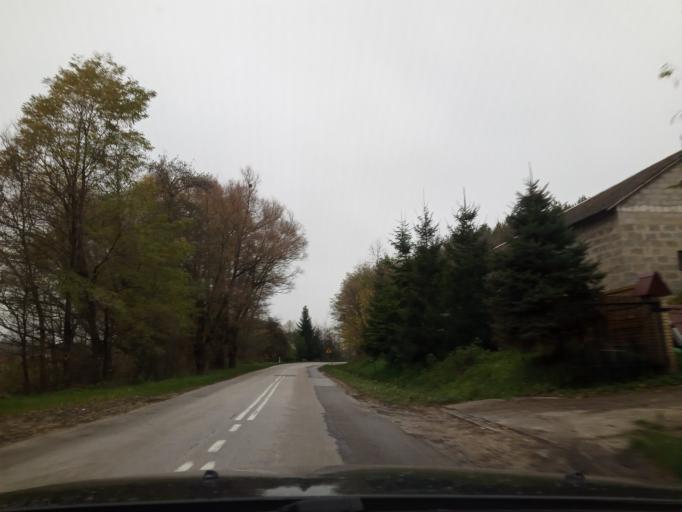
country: PL
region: Swietokrzyskie
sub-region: Powiat pinczowski
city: Dzialoszyce
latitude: 50.3994
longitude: 20.3232
